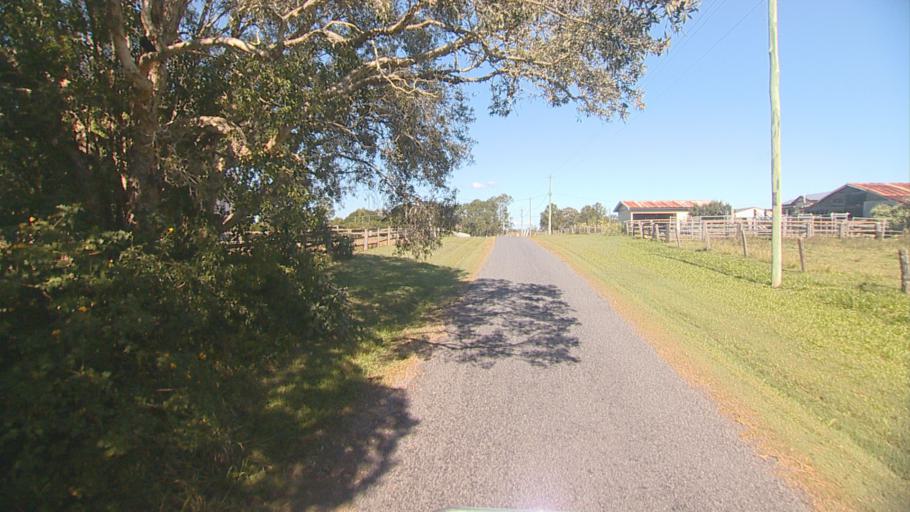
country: AU
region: Queensland
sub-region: Gold Coast
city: Yatala
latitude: -27.6867
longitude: 153.2245
